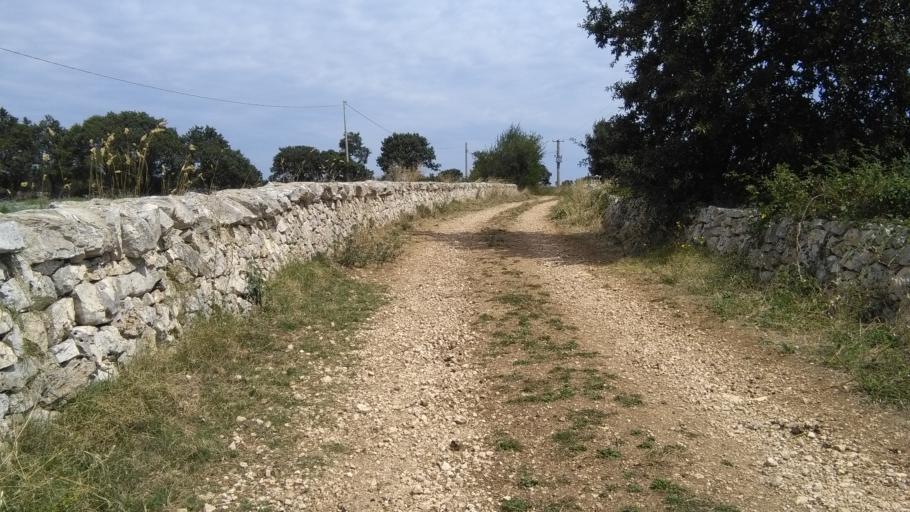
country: IT
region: Apulia
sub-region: Provincia di Bari
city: Gioia del Colle
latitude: 40.8264
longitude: 16.9838
